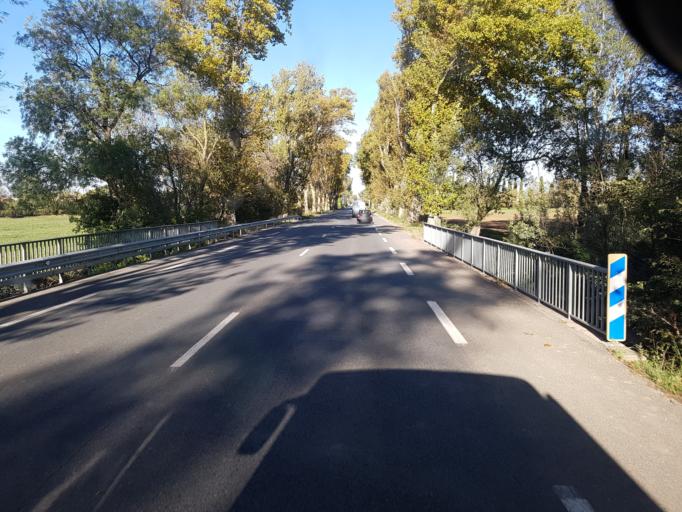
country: FR
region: Languedoc-Roussillon
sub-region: Departement de l'Aude
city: Coursan
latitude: 43.2237
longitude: 3.0436
